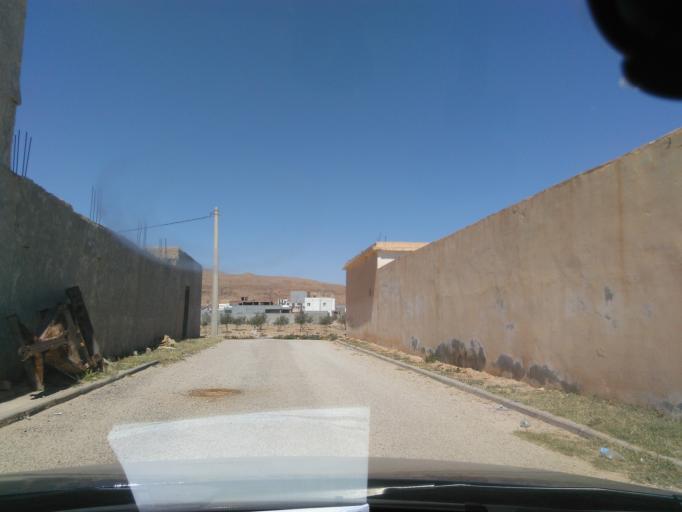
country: TN
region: Tataouine
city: Tataouine
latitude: 32.9488
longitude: 10.4629
